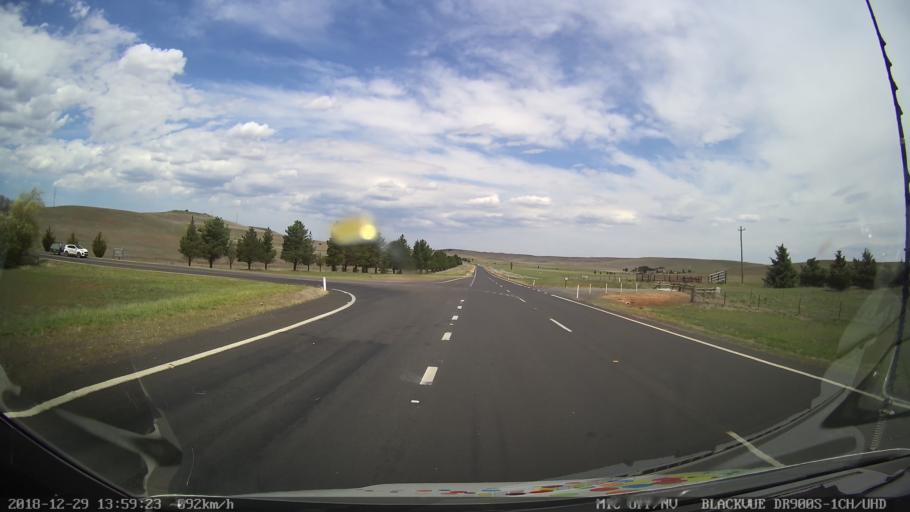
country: AU
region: New South Wales
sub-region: Cooma-Monaro
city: Cooma
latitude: -36.2514
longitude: 149.1486
